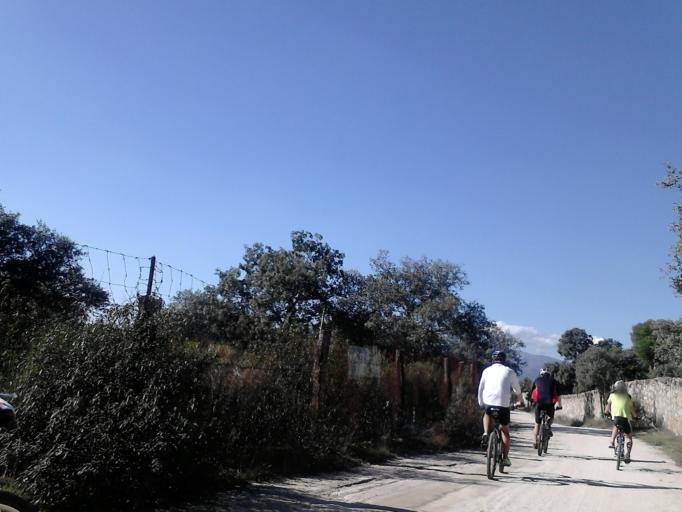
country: ES
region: Madrid
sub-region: Provincia de Madrid
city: Galapagar
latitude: 40.5600
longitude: -3.9880
